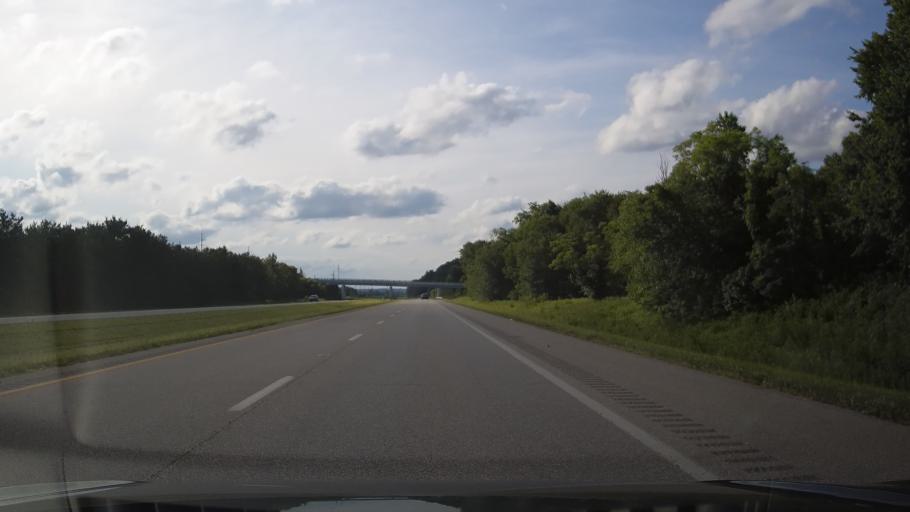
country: US
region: Ohio
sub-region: Scioto County
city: Franklin Furnace
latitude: 38.6203
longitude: -82.8339
